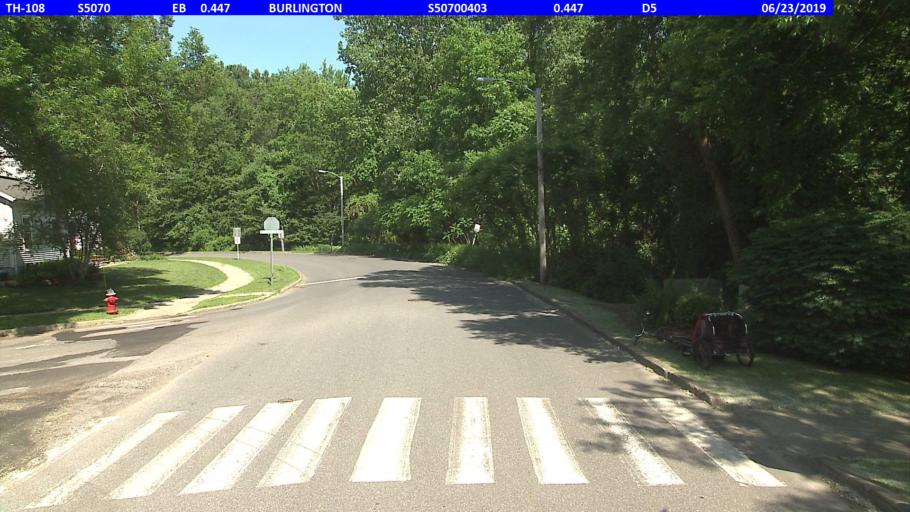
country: US
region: Vermont
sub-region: Chittenden County
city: Burlington
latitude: 44.5051
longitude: -73.2640
